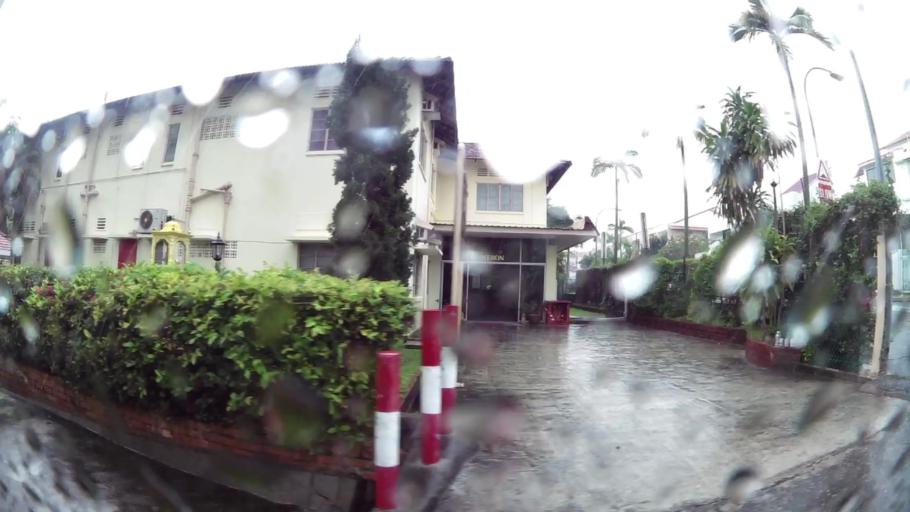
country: SG
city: Singapore
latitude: 1.3369
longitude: 103.9551
